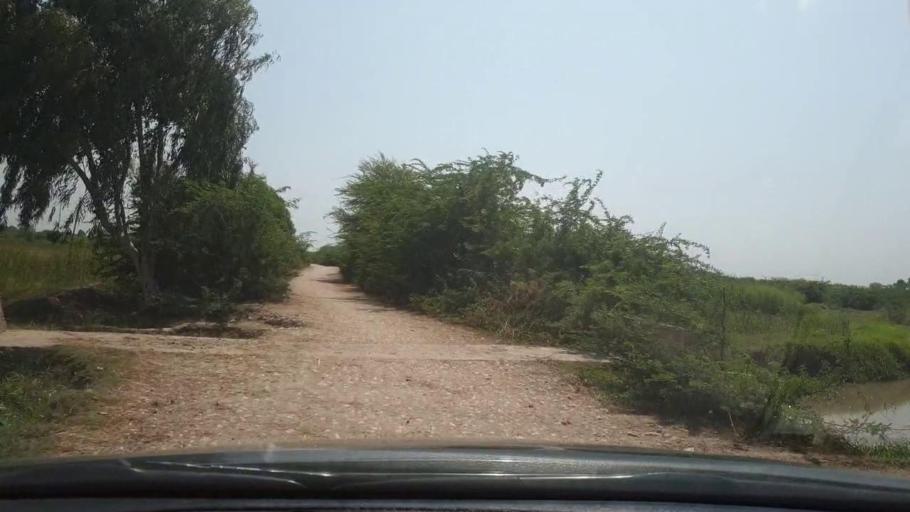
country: PK
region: Sindh
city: Tando Bago
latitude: 24.7770
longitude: 69.1833
